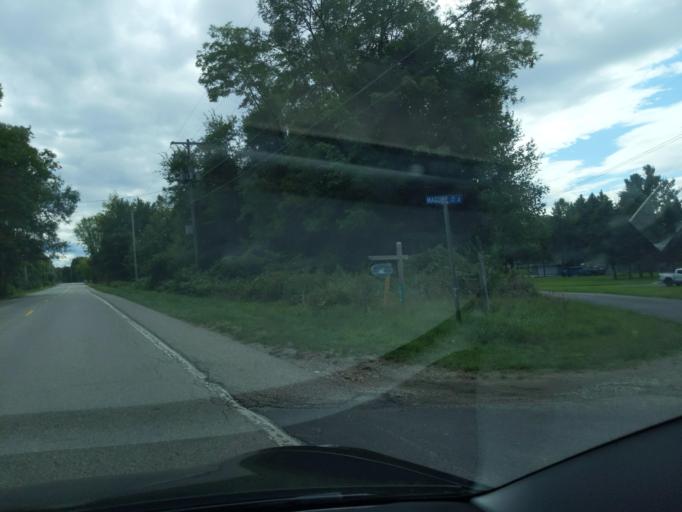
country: US
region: Michigan
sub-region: Kalkaska County
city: Rapid City
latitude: 44.9208
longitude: -85.2856
